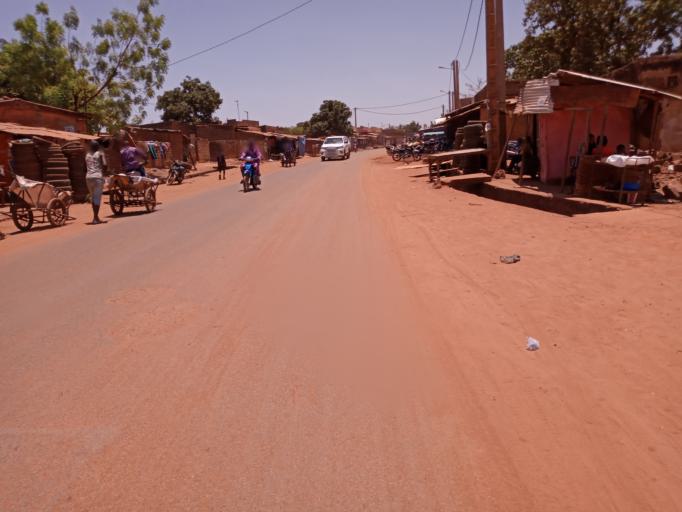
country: ML
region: Bamako
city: Bamako
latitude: 12.5780
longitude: -7.9713
